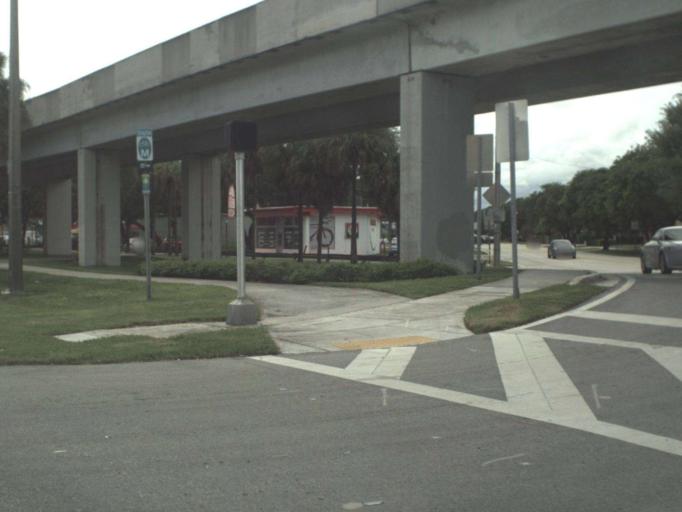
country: US
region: Florida
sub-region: Miami-Dade County
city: South Miami
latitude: 25.6964
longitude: -80.2994
